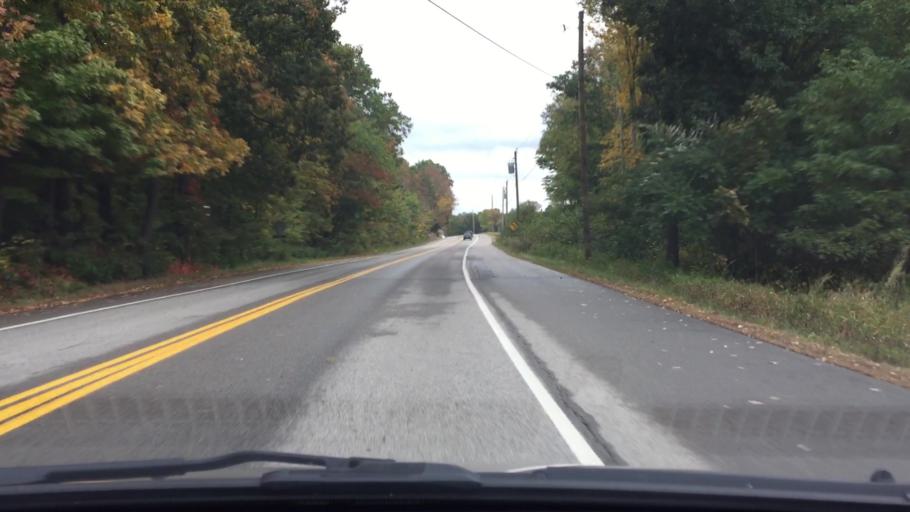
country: US
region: New Hampshire
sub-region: Strafford County
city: Durham
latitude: 43.1326
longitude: -70.8819
